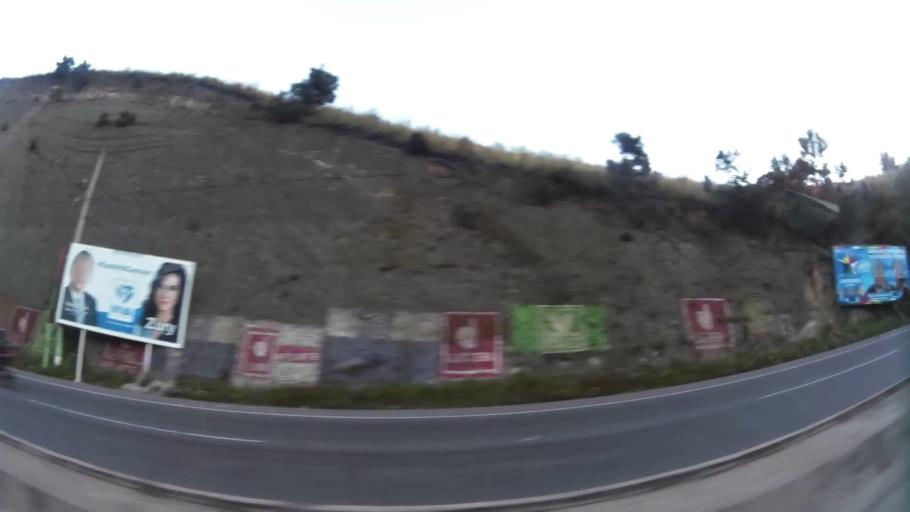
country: GT
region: Quetzaltenango
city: Salcaja
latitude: 14.8634
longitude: -91.4726
